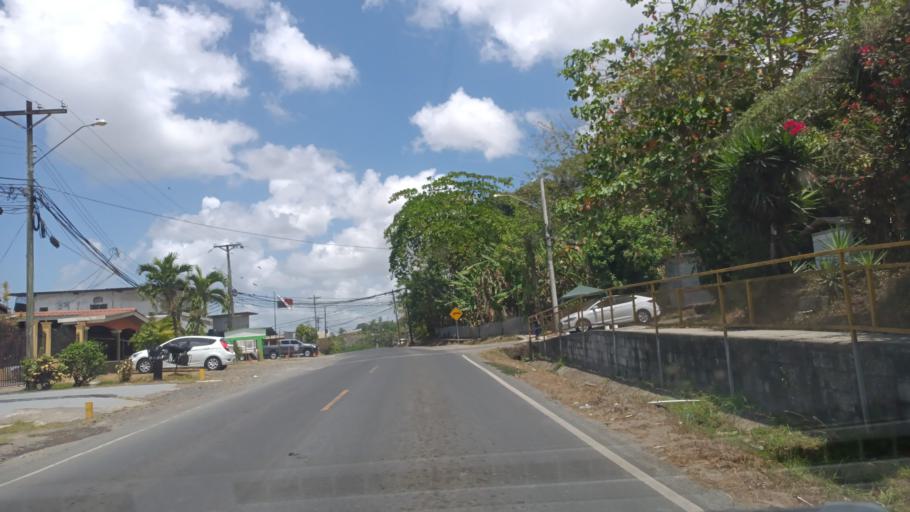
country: PA
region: Panama
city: Alcalde Diaz
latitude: 9.1098
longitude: -79.5622
